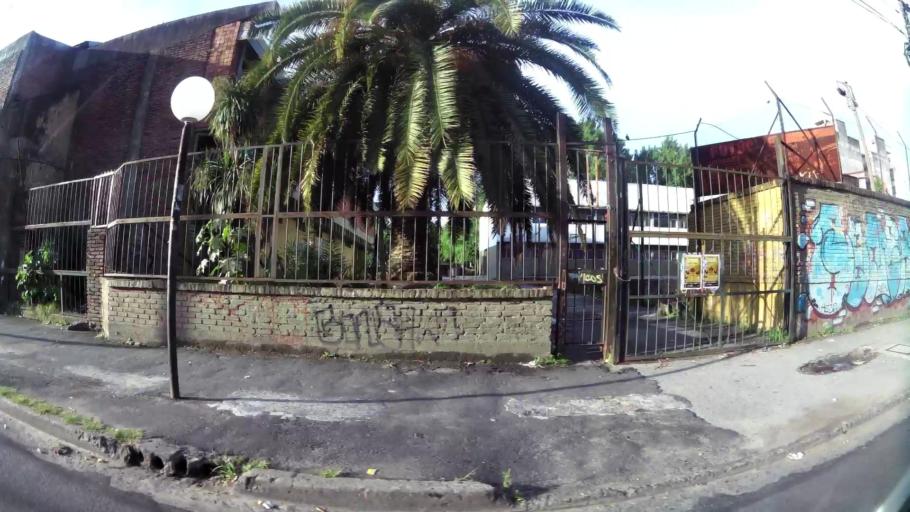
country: AR
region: Buenos Aires
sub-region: Partido de Moron
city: Moron
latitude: -34.6503
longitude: -58.6248
